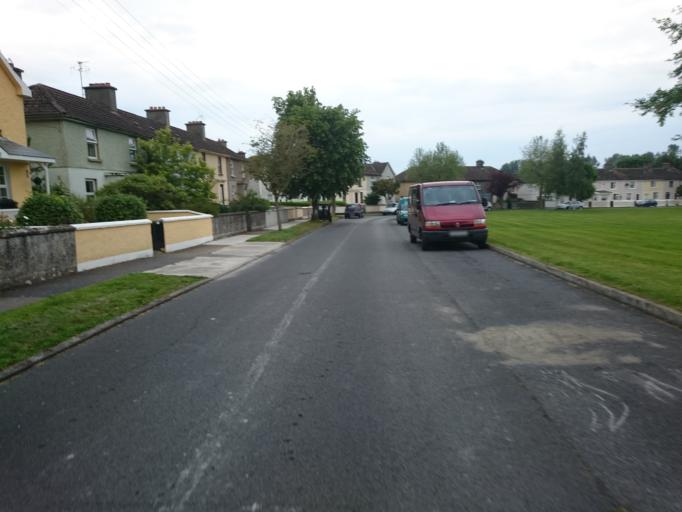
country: IE
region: Leinster
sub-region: Kilkenny
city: Kilkenny
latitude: 52.6507
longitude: -7.2643
